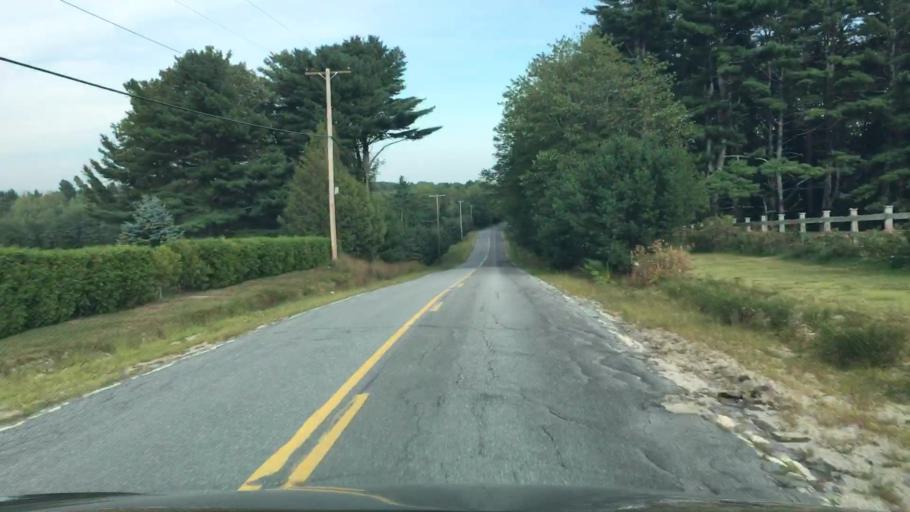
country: US
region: Maine
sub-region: Hancock County
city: Surry
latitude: 44.4995
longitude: -68.5525
